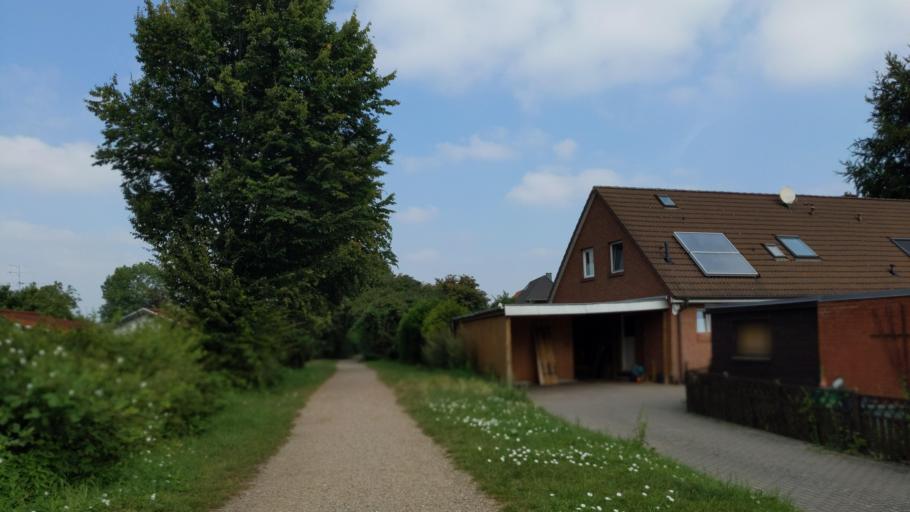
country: DE
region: Schleswig-Holstein
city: Stockelsdorf
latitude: 53.8746
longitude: 10.6322
